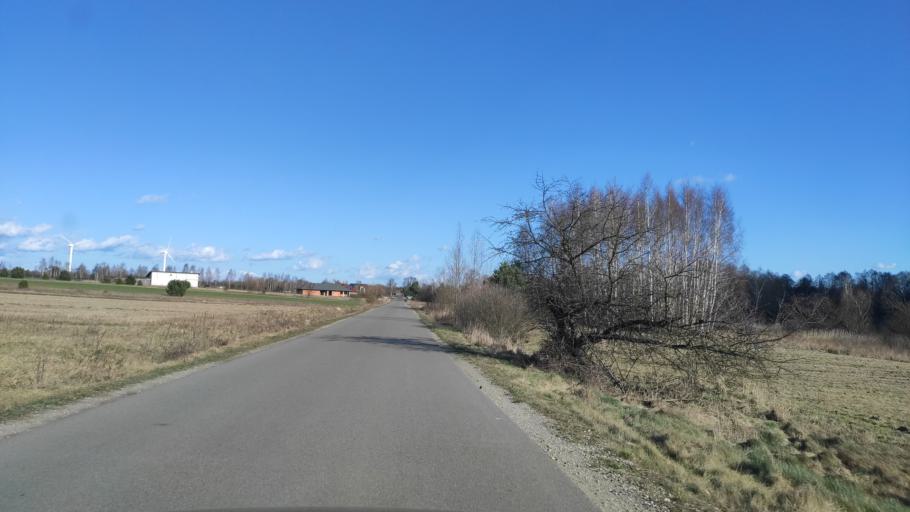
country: PL
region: Masovian Voivodeship
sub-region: Powiat radomski
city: Jastrzebia
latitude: 51.4529
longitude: 21.2397
